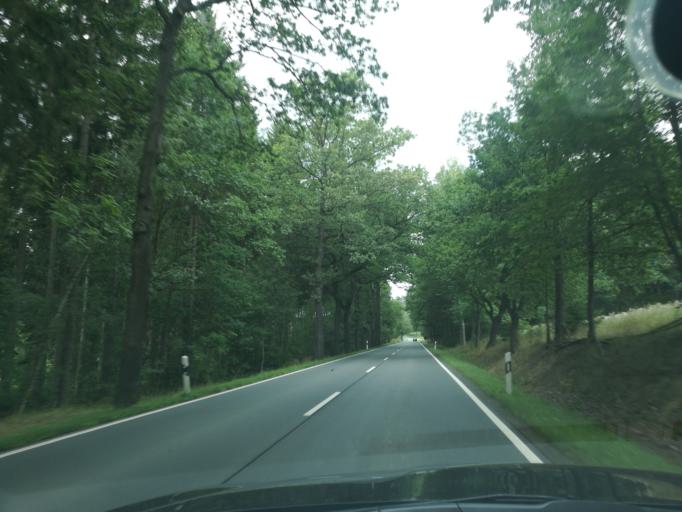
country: DE
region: Saxony
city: Eichigt
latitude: 50.3765
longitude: 12.2053
